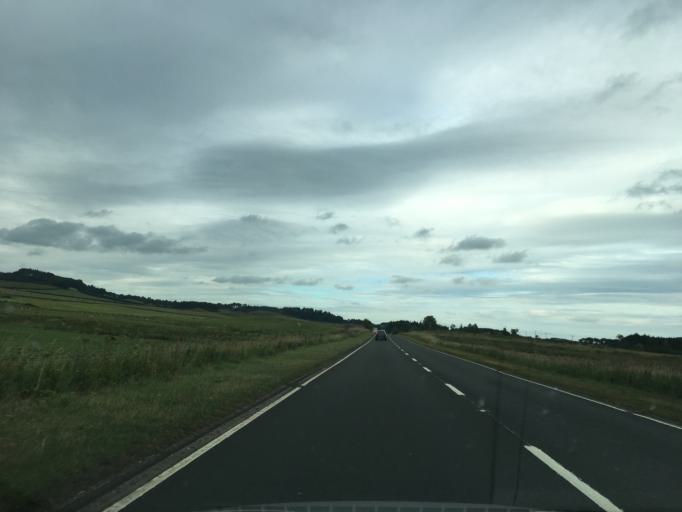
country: GB
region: Scotland
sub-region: The Scottish Borders
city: West Linton
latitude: 55.7225
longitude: -3.4007
